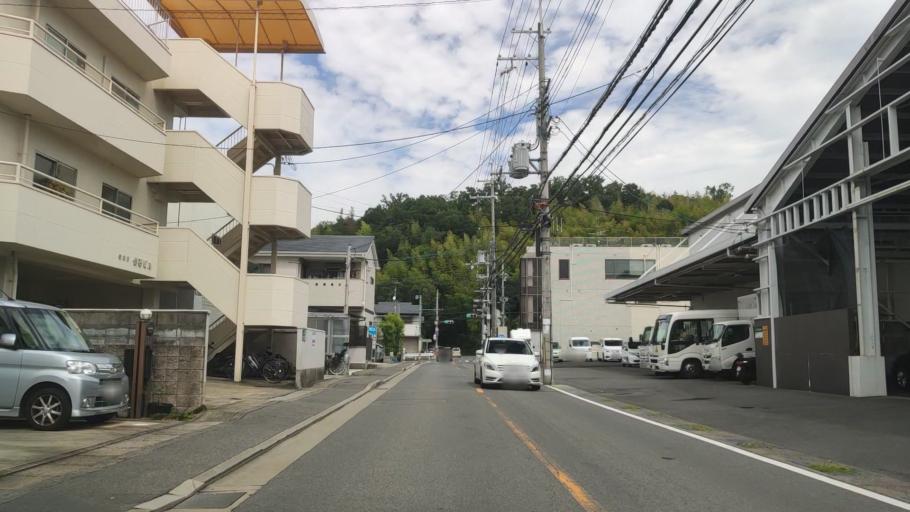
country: JP
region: Kyoto
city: Kyoto
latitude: 35.0228
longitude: 135.6982
